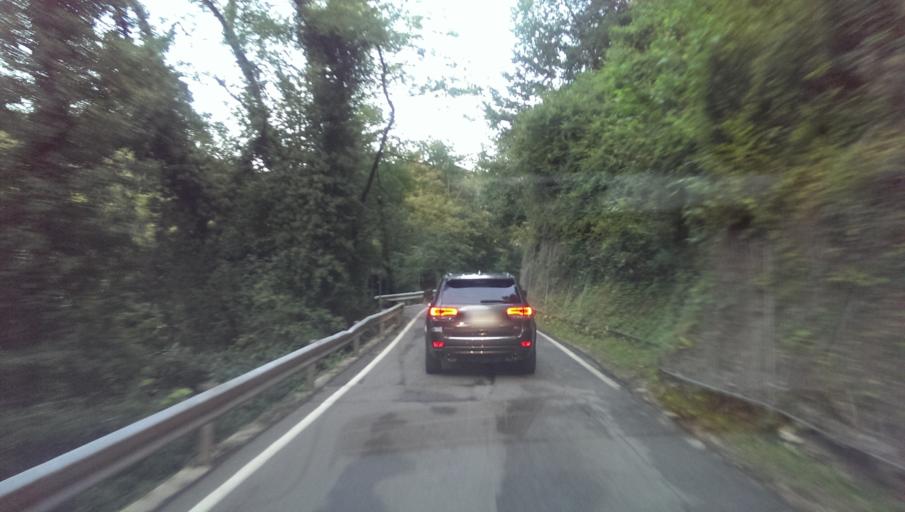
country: IT
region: Lombardy
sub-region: Provincia di Brescia
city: Pieve
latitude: 45.7777
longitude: 10.7568
